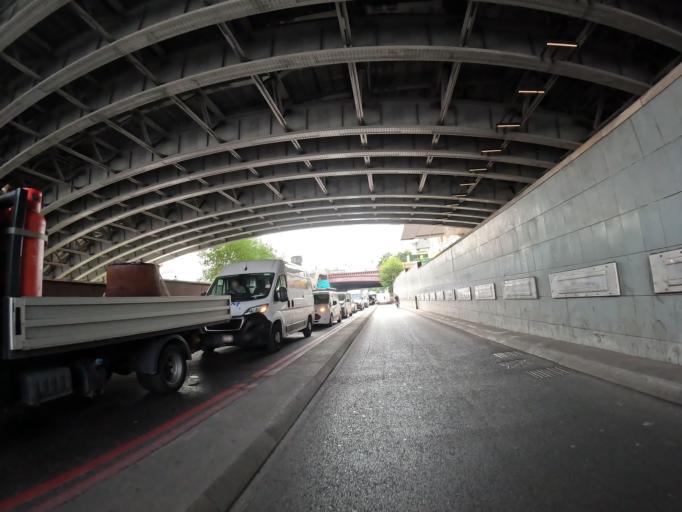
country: GB
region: England
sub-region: Greater London
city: Islington
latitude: 51.5422
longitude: -0.0866
